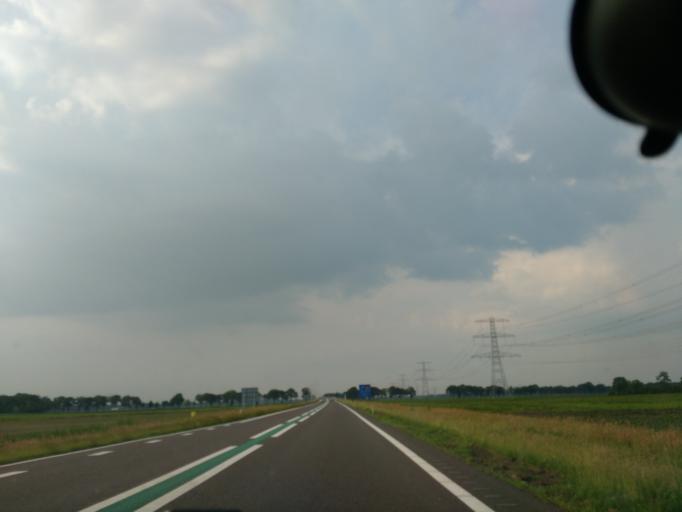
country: NL
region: Drenthe
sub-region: Gemeente Coevorden
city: Sleen
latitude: 52.7790
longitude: 6.8455
